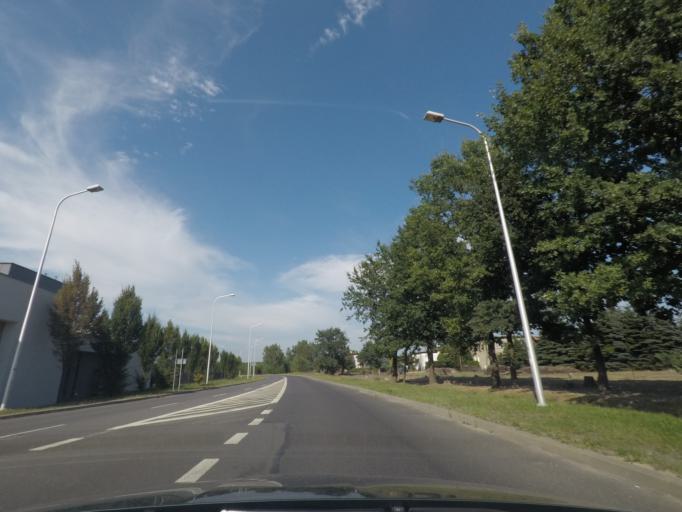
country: PL
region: Silesian Voivodeship
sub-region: Zory
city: Zory
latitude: 50.0553
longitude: 18.6817
